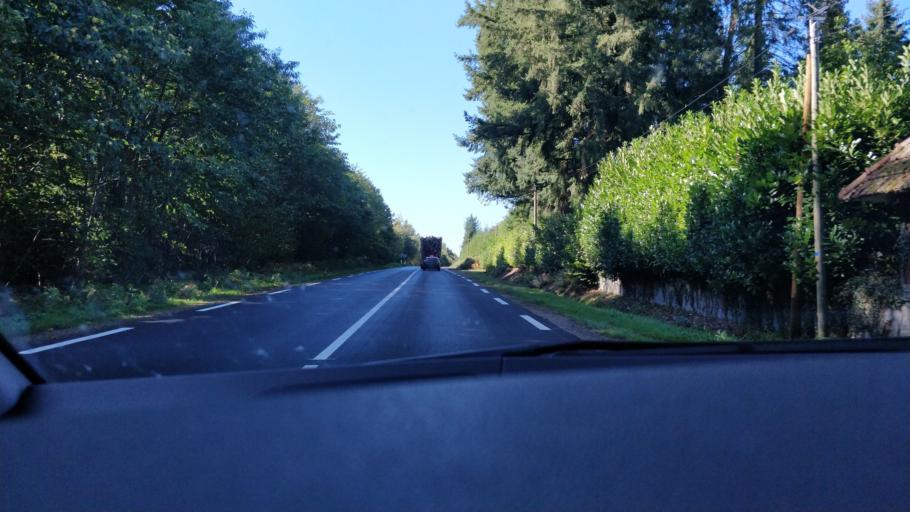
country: FR
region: Limousin
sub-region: Departement de la Haute-Vienne
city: Saint-Leonard-de-Noblat
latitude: 45.8756
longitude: 1.5420
